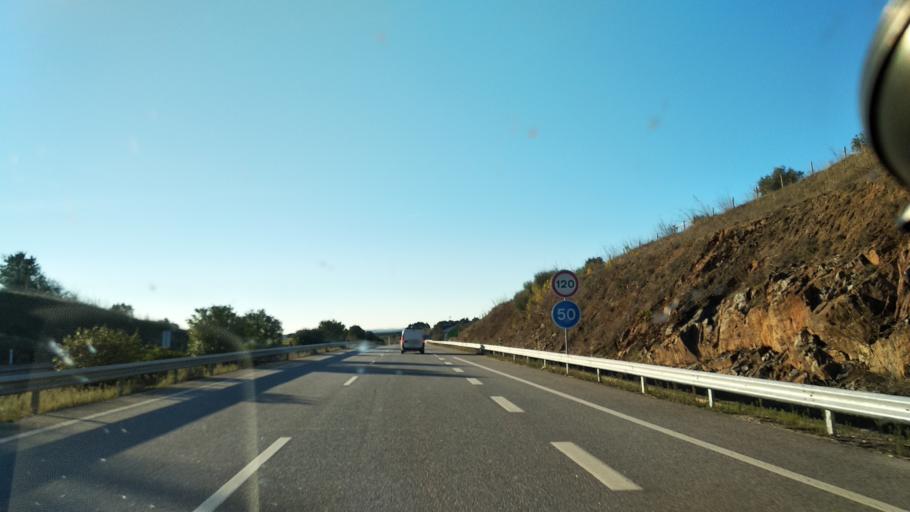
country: PT
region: Santarem
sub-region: Abrantes
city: Alferrarede
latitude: 39.4929
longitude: -8.1059
